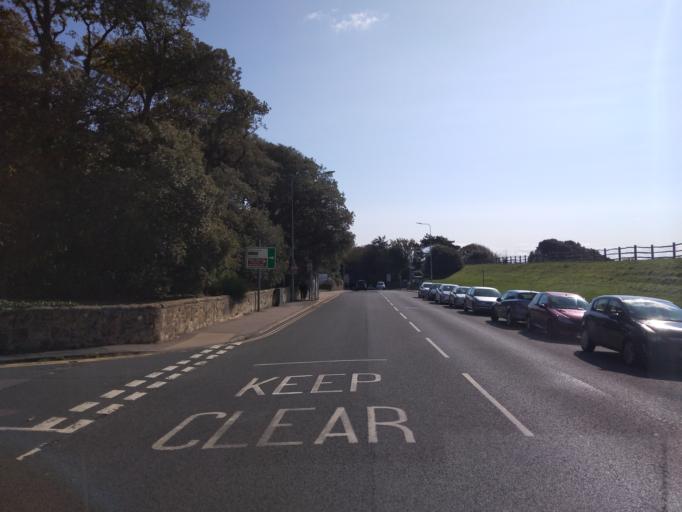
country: GB
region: England
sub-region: East Sussex
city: Hastings
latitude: 50.8571
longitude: 0.5681
